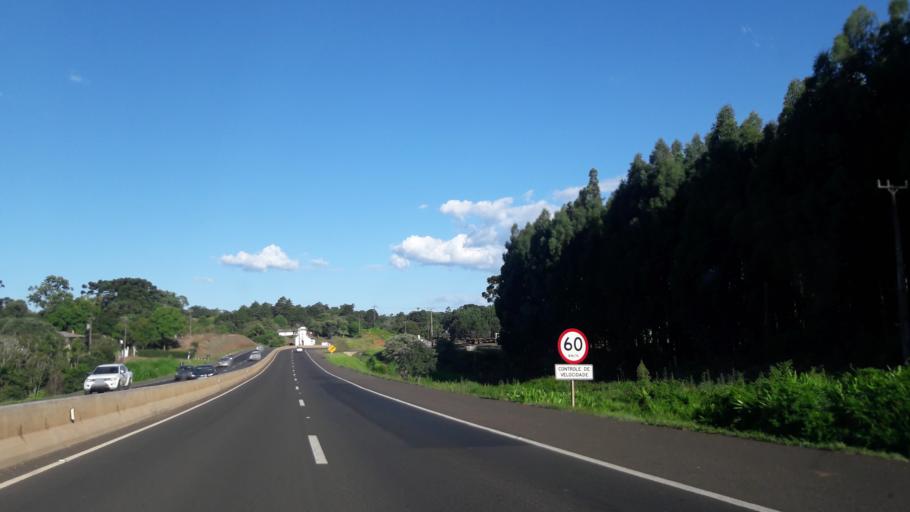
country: BR
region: Parana
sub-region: Guarapuava
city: Guarapuava
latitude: -25.3444
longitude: -51.3961
